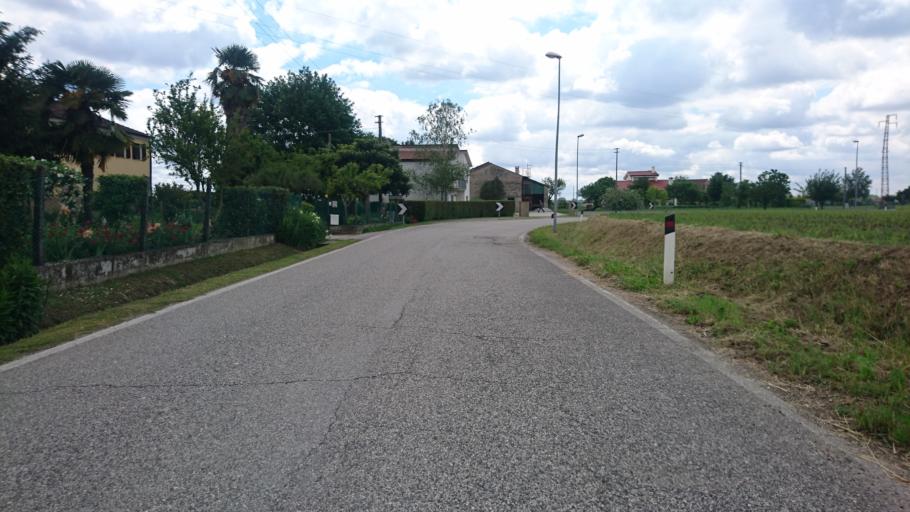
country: IT
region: Veneto
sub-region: Provincia di Padova
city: Villa Estense
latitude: 45.1584
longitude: 11.6547
